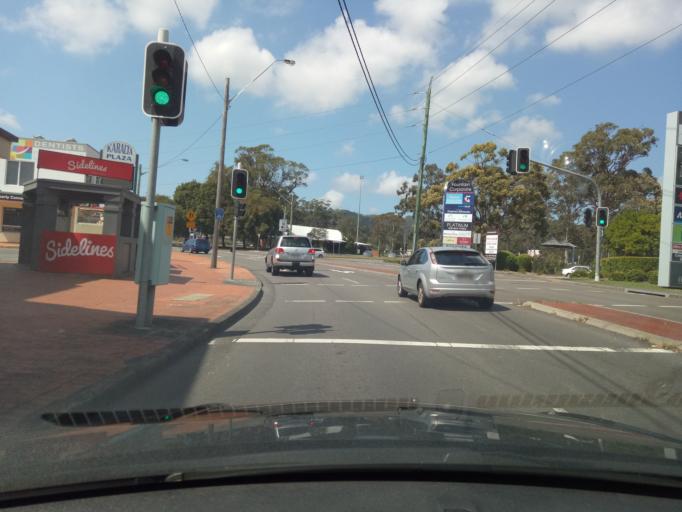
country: AU
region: New South Wales
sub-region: Gosford Shire
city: Erina
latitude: -33.4385
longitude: 151.3844
